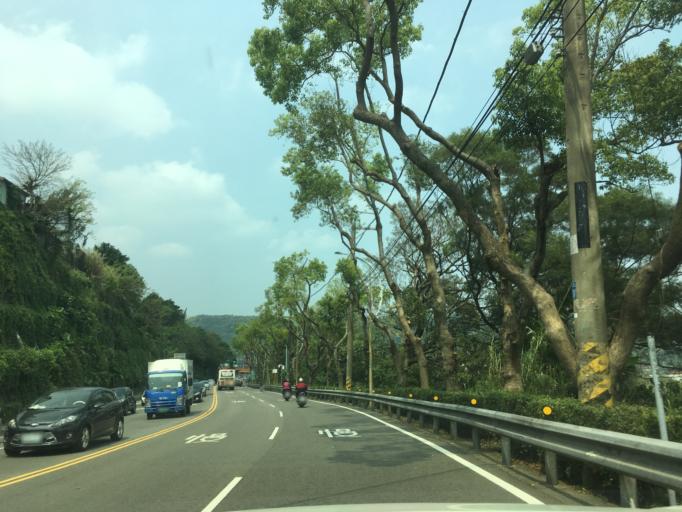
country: TW
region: Taiwan
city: Daxi
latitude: 24.8859
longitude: 121.2885
